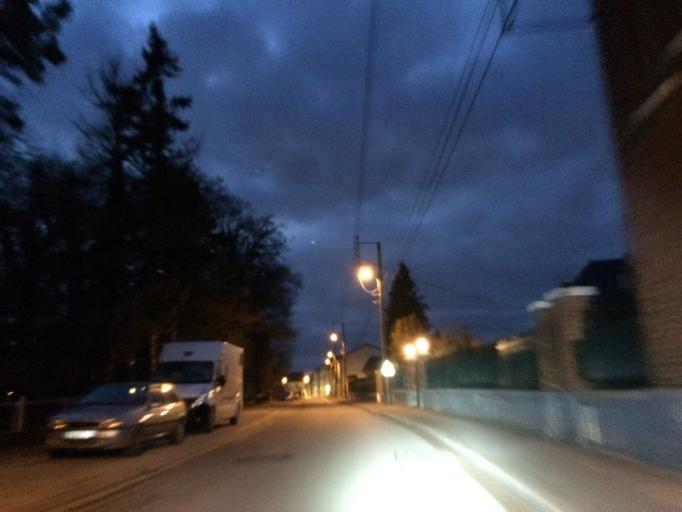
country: FR
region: Picardie
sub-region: Departement de l'Oise
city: Lamorlaye
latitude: 49.1547
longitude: 2.4475
